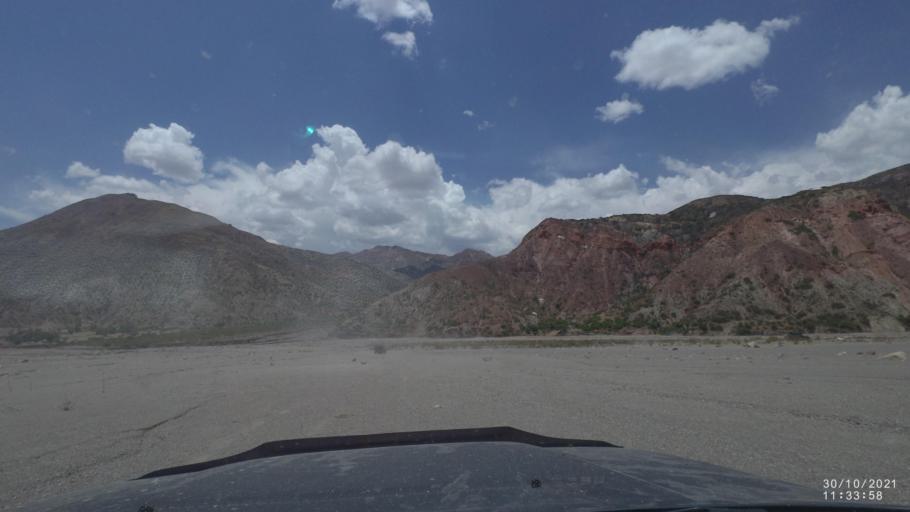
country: BO
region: Cochabamba
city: Sipe Sipe
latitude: -17.5231
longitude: -66.5922
